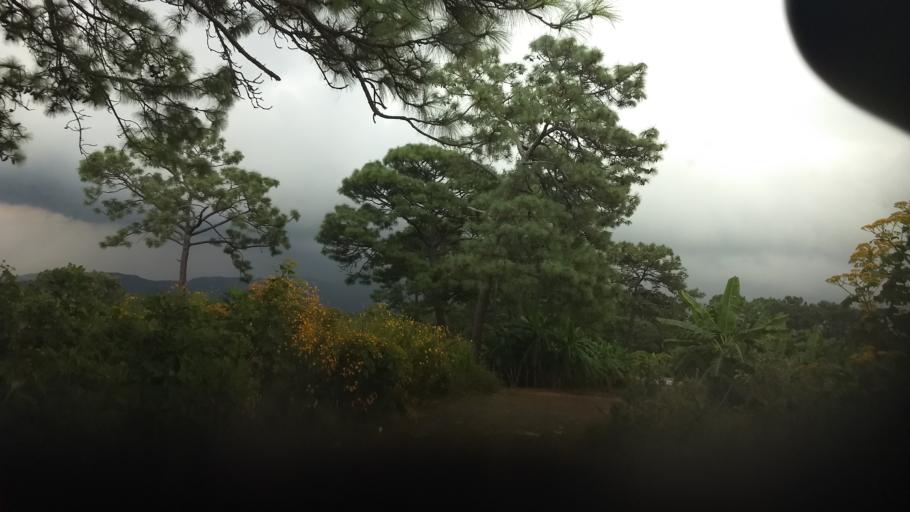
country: MX
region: Jalisco
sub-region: Tonila
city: San Marcos
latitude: 19.4662
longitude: -103.5329
